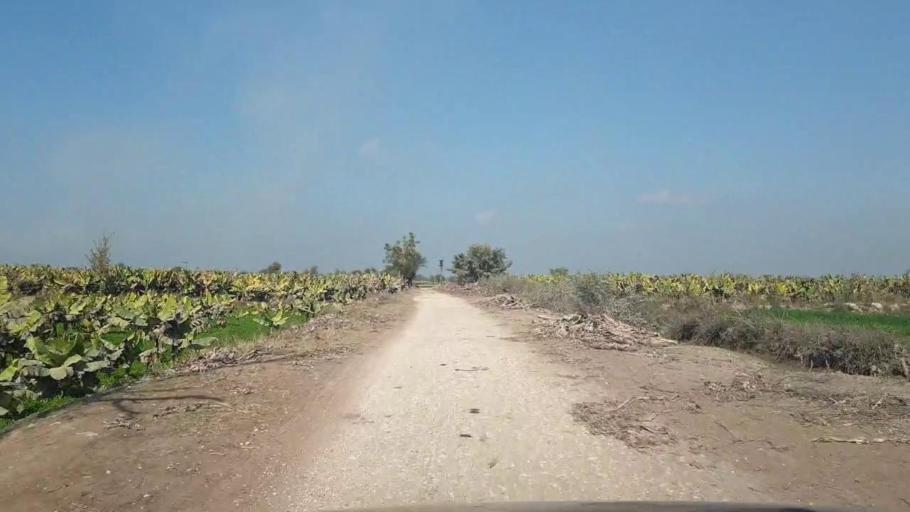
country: PK
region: Sindh
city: Shahdadpur
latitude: 25.9240
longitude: 68.5868
